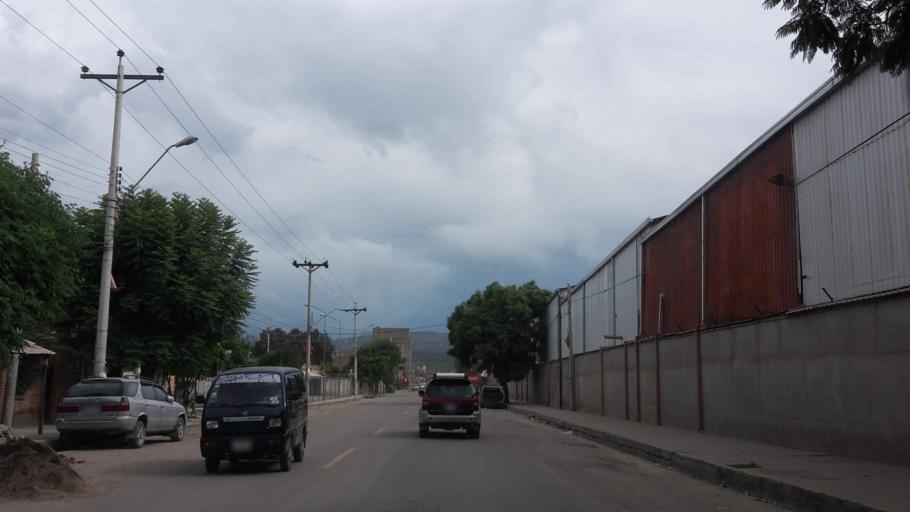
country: BO
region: Cochabamba
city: Cochabamba
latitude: -17.3880
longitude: -66.2506
